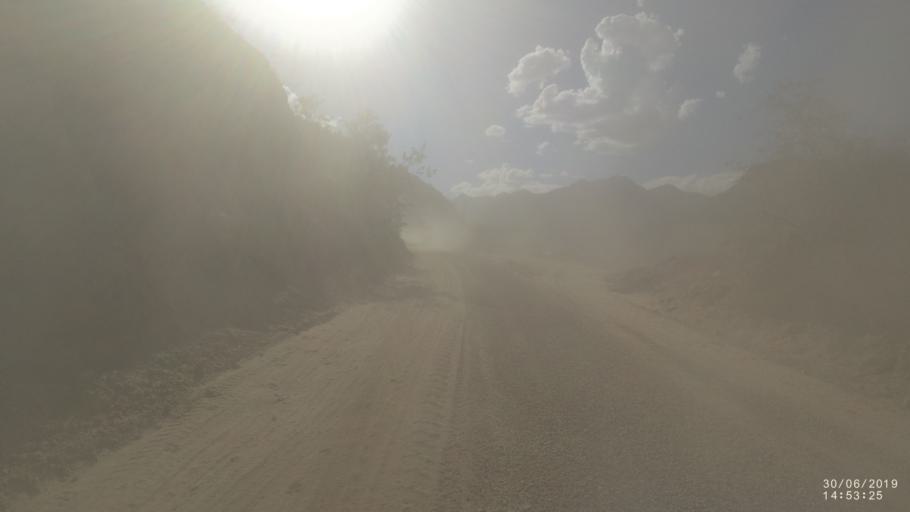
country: BO
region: Cochabamba
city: Irpa Irpa
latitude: -17.7638
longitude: -66.3483
